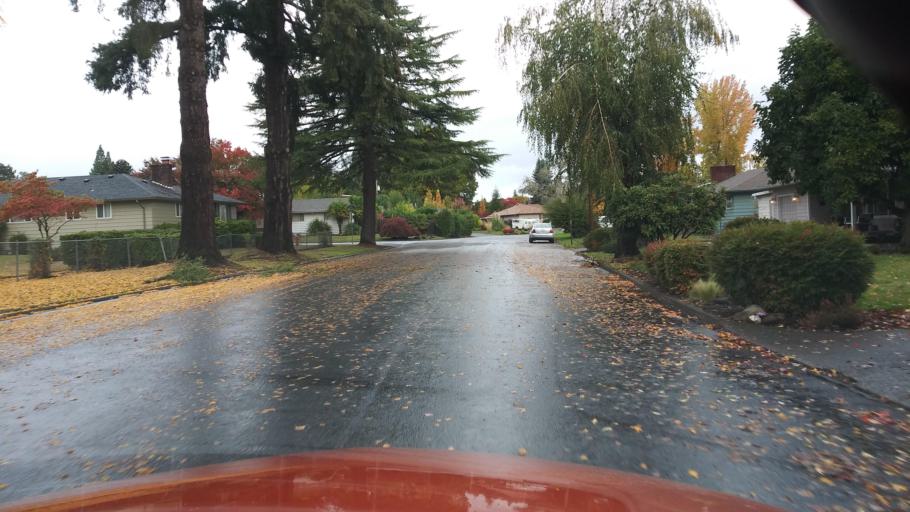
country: US
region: Oregon
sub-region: Washington County
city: Forest Grove
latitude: 45.5126
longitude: -123.0983
